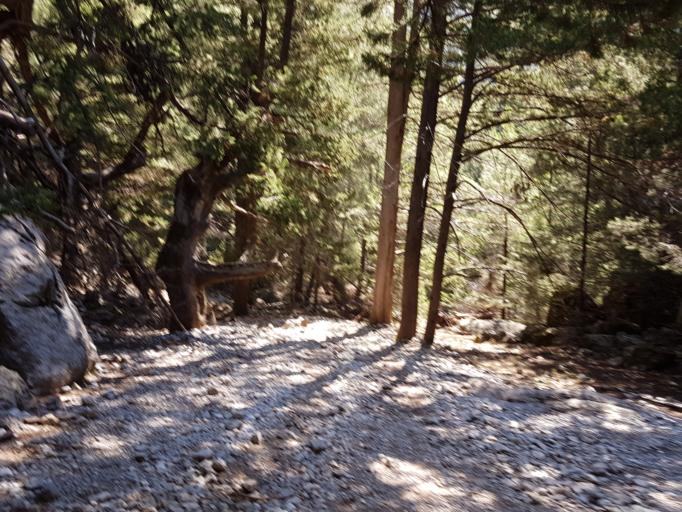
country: GR
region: Crete
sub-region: Nomos Chanias
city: Perivolia
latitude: 35.3059
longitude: 23.9375
